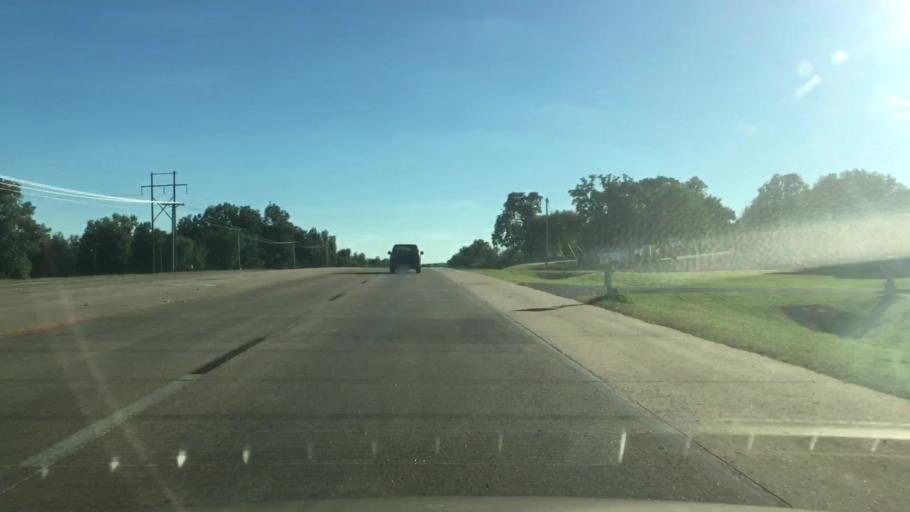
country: US
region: Oklahoma
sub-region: Cherokee County
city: Park Hill
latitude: 35.8322
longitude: -95.0425
